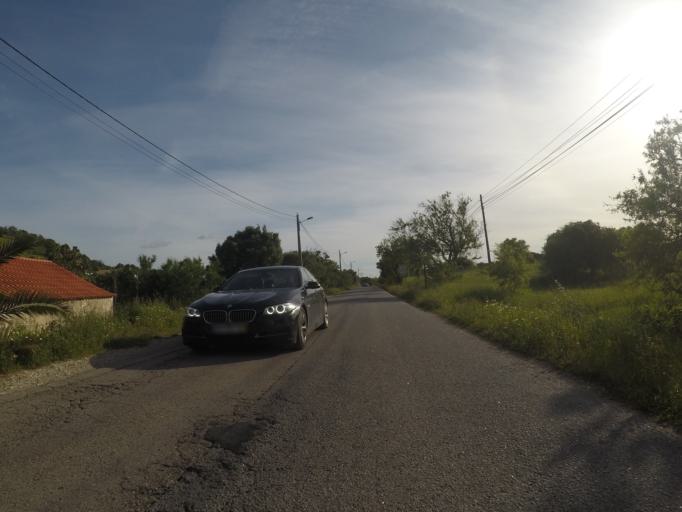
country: PT
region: Faro
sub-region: Lagos
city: Lagos
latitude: 37.1020
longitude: -8.7135
